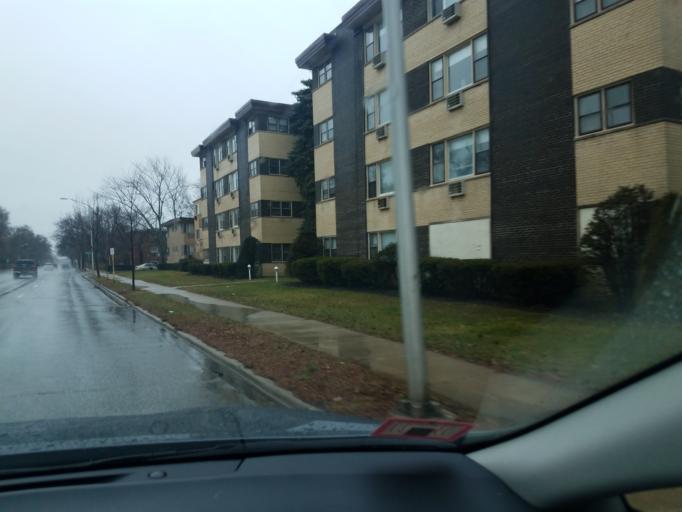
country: US
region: Illinois
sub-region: Cook County
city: Skokie
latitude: 42.0389
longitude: -87.7472
